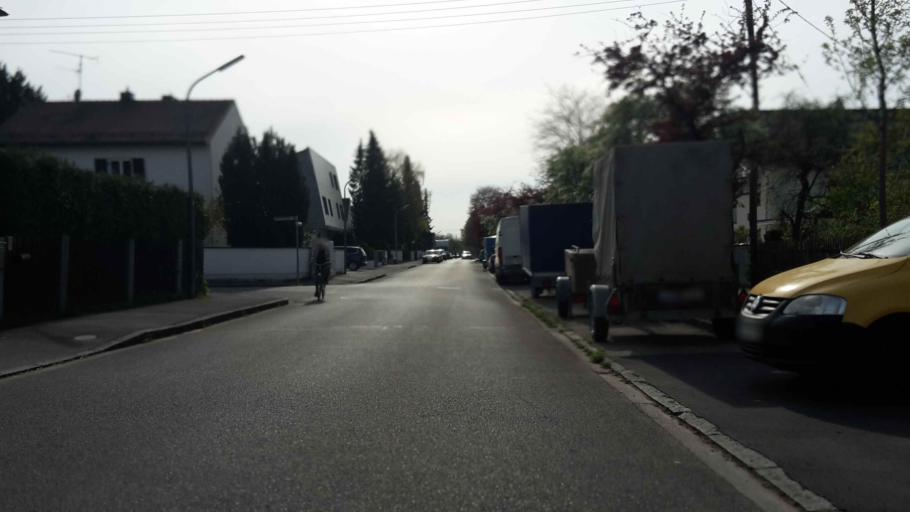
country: DE
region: Bavaria
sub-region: Upper Bavaria
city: Karlsfeld
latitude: 48.1872
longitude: 11.4496
